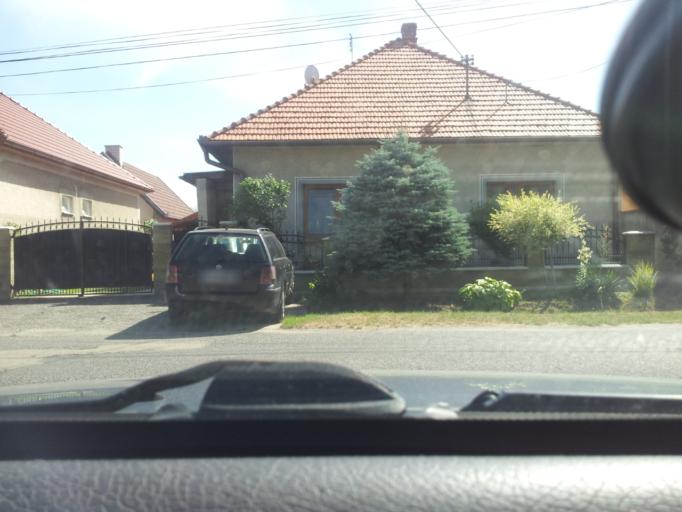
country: SK
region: Nitriansky
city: Tlmace
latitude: 48.2444
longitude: 18.5282
